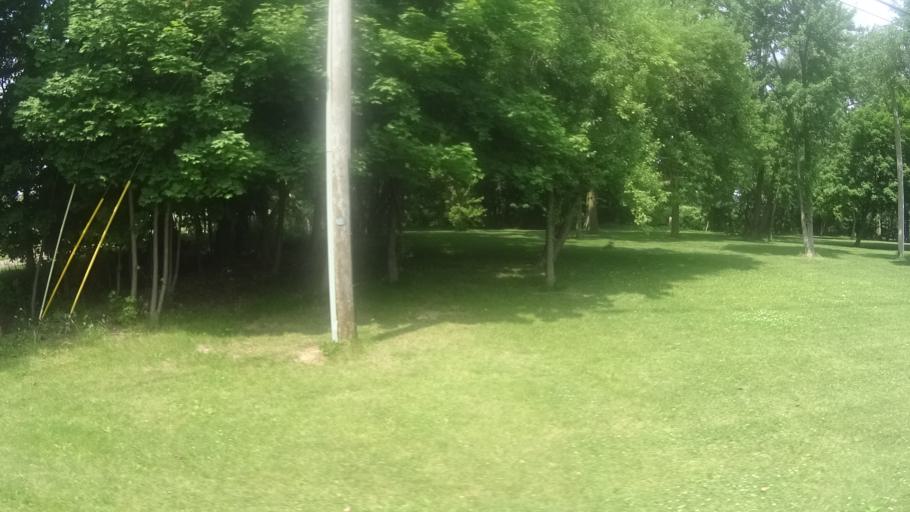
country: US
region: Ohio
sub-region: Huron County
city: Monroeville
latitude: 41.3372
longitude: -82.6937
